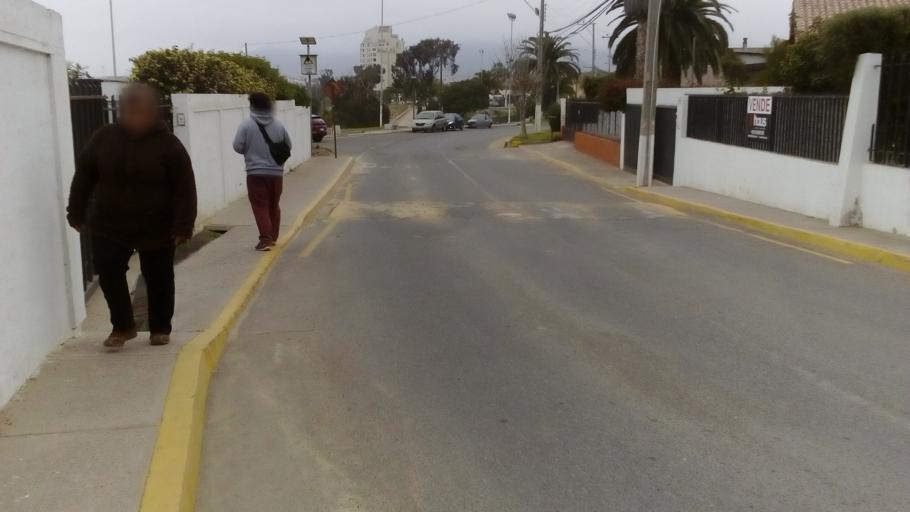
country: CL
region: Coquimbo
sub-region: Provincia de Elqui
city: Coquimbo
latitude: -29.9837
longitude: -71.3666
